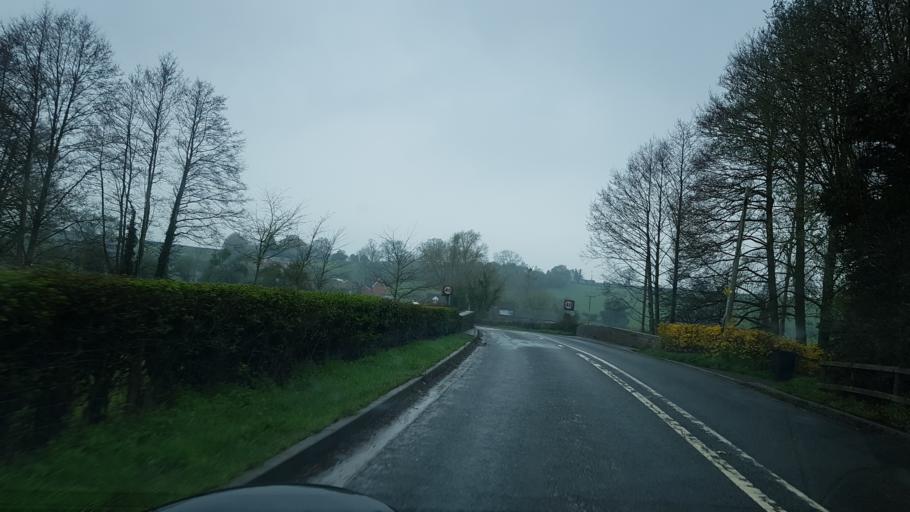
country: GB
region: England
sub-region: Herefordshire
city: Moreton Jeffries
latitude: 52.1414
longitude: -2.5582
